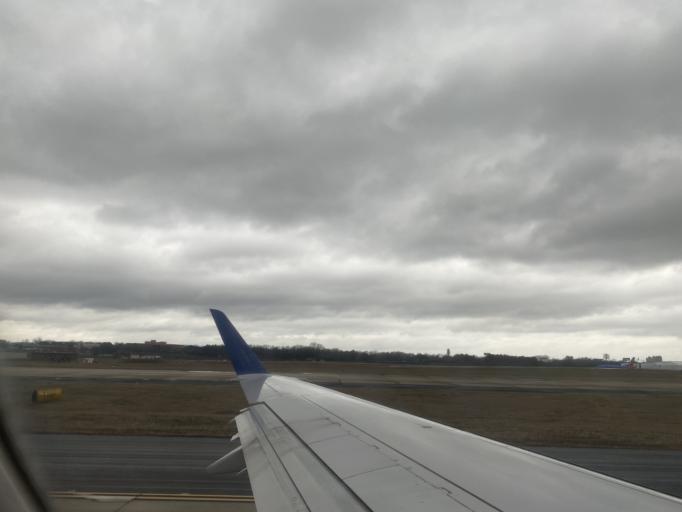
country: US
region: Georgia
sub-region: Fulton County
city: College Park
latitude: 33.6443
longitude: -84.4396
